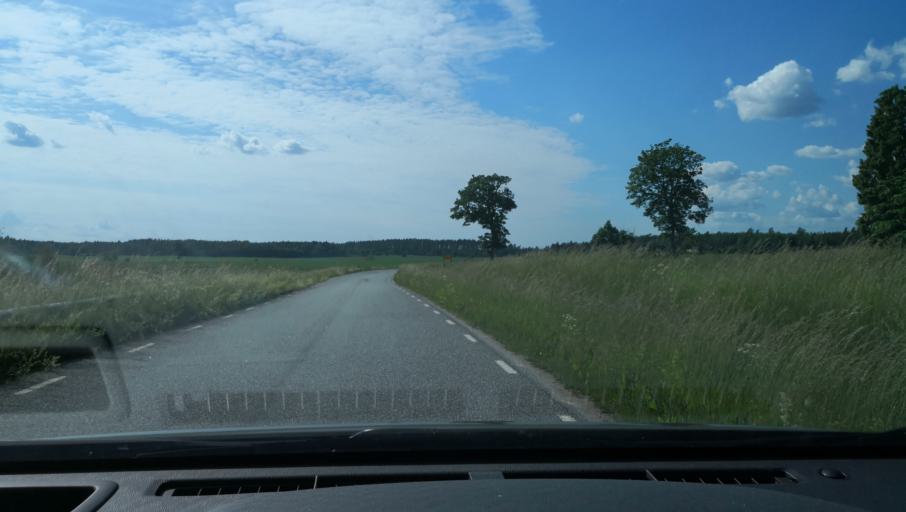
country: SE
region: Uppsala
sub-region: Enkopings Kommun
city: Orsundsbro
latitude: 59.8356
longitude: 17.3058
